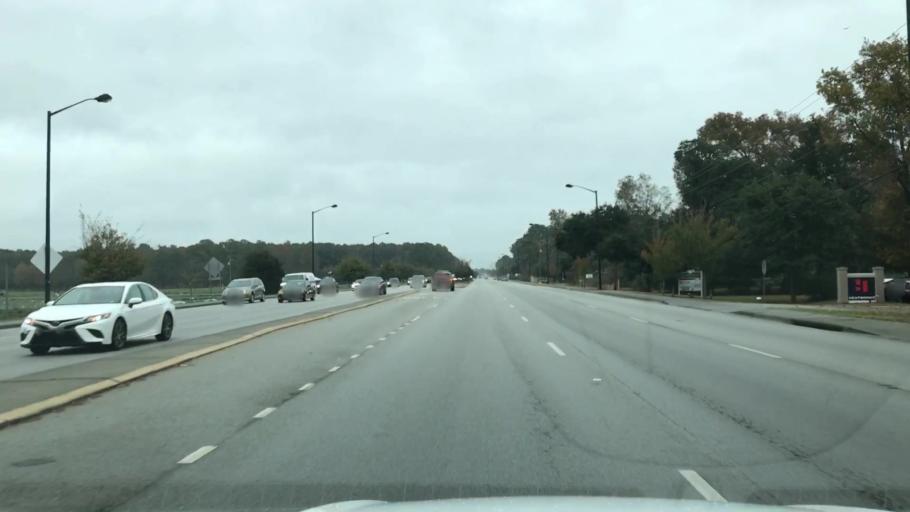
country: US
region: South Carolina
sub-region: Charleston County
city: Isle of Palms
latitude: 32.8459
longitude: -79.8123
